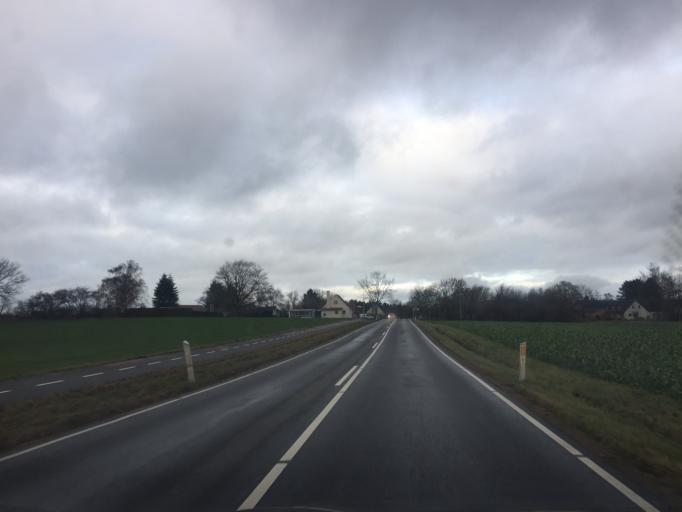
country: DK
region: Zealand
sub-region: Holbaek Kommune
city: Tollose
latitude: 55.6055
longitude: 11.7062
